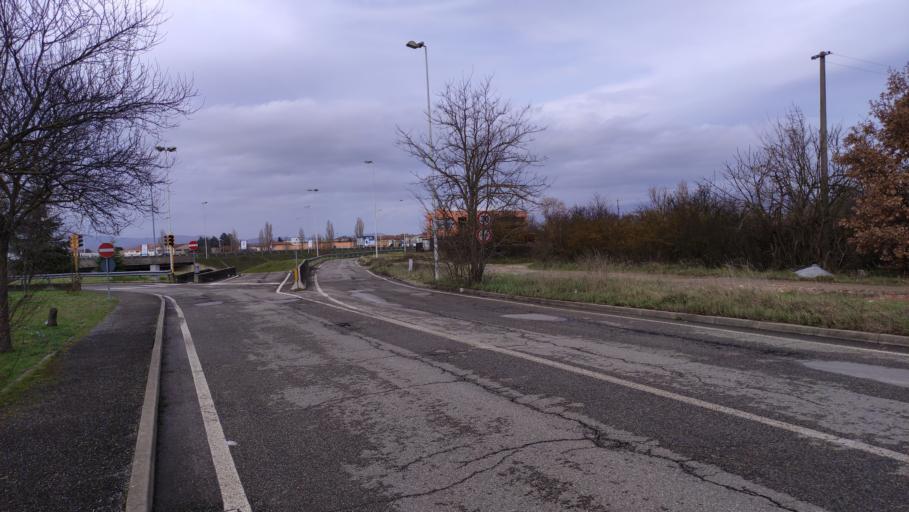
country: IT
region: Tuscany
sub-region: Province of Arezzo
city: Arezzo
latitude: 43.4733
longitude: 11.8648
